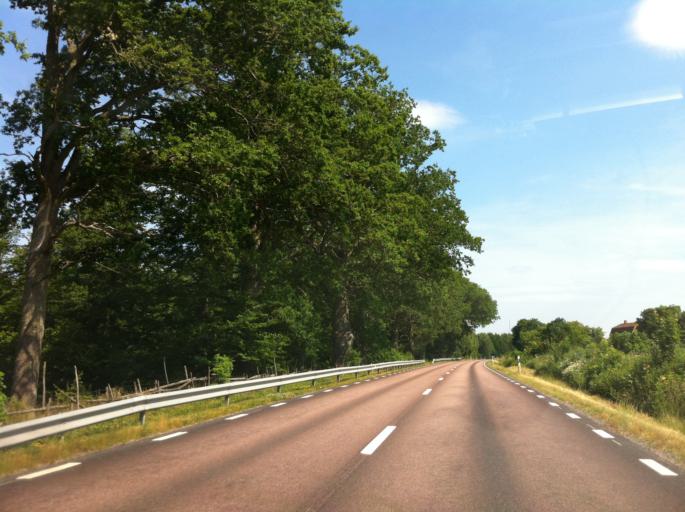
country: SE
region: Kalmar
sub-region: Nybro Kommun
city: Nybro
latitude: 56.7819
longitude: 15.8249
